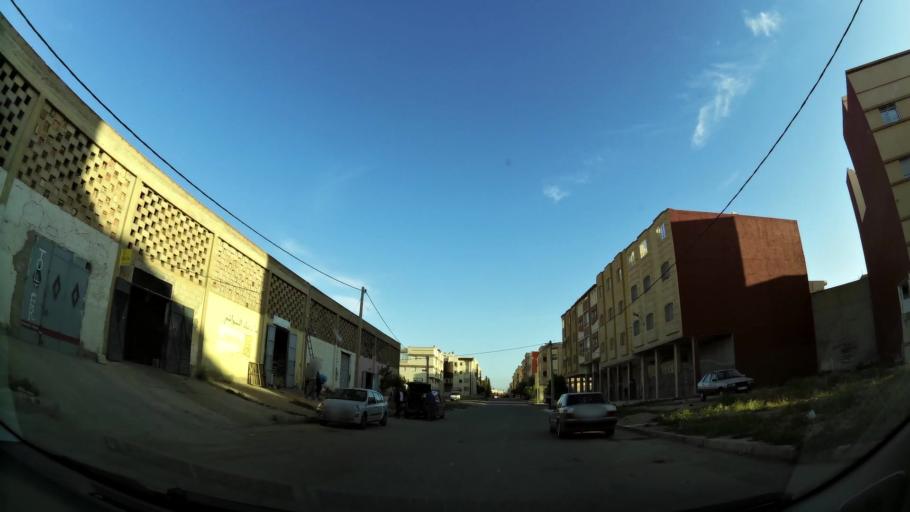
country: MA
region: Oriental
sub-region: Oujda-Angad
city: Oujda
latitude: 34.7007
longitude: -1.9163
